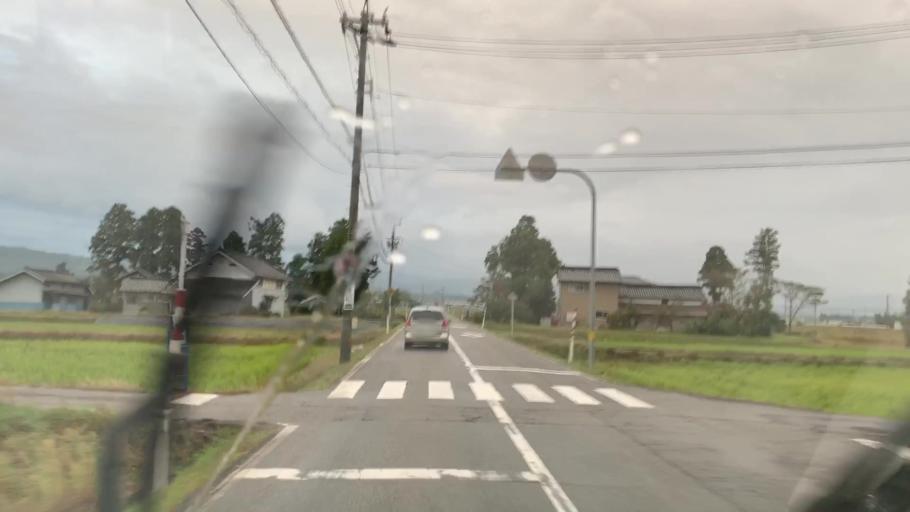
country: JP
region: Toyama
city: Kamiichi
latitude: 36.6443
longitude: 137.3285
